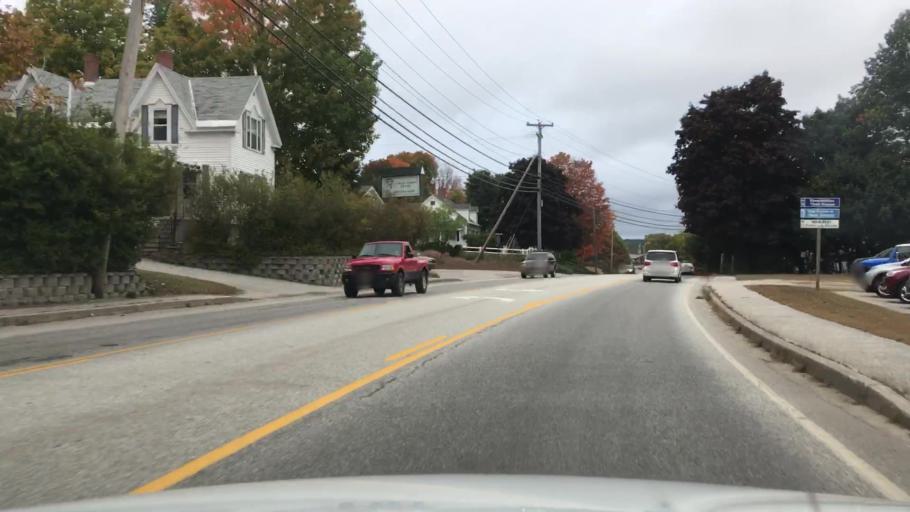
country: US
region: Maine
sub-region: Oxford County
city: Norway
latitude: 44.2039
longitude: -70.5317
